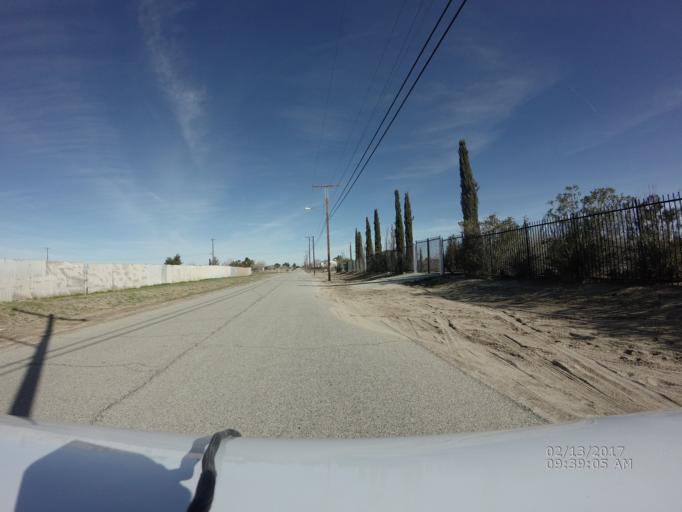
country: US
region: California
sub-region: Los Angeles County
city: Littlerock
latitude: 34.5496
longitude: -117.9669
